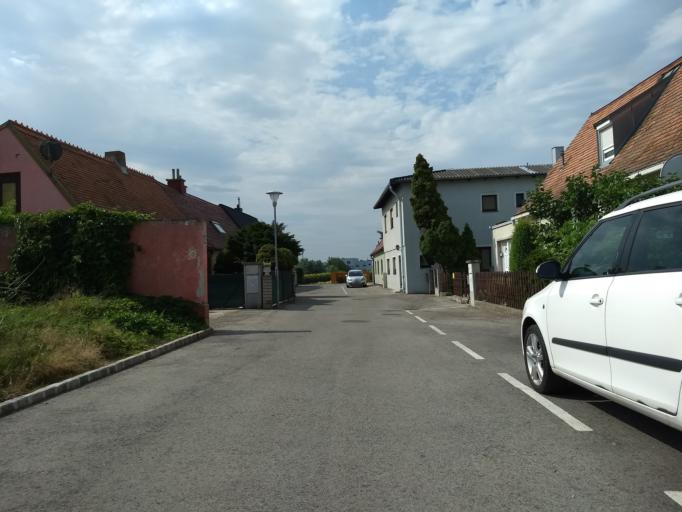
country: AT
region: Lower Austria
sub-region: Politischer Bezirk Modling
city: Neu-Guntramsdorf
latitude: 48.0627
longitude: 16.3212
